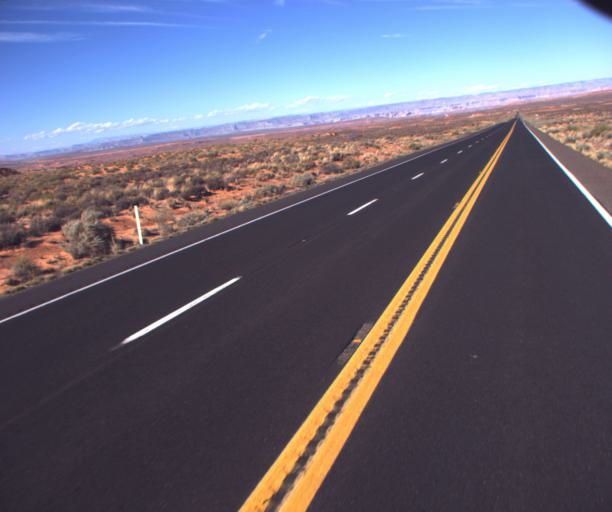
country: US
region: Arizona
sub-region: Coconino County
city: LeChee
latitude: 36.8056
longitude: -111.5203
